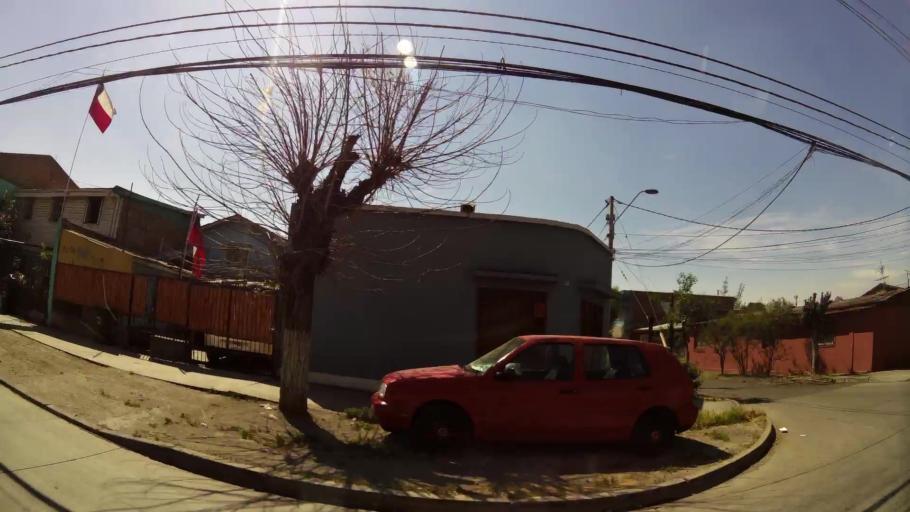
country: CL
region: Santiago Metropolitan
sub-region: Provincia de Santiago
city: La Pintana
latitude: -33.5250
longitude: -70.6393
